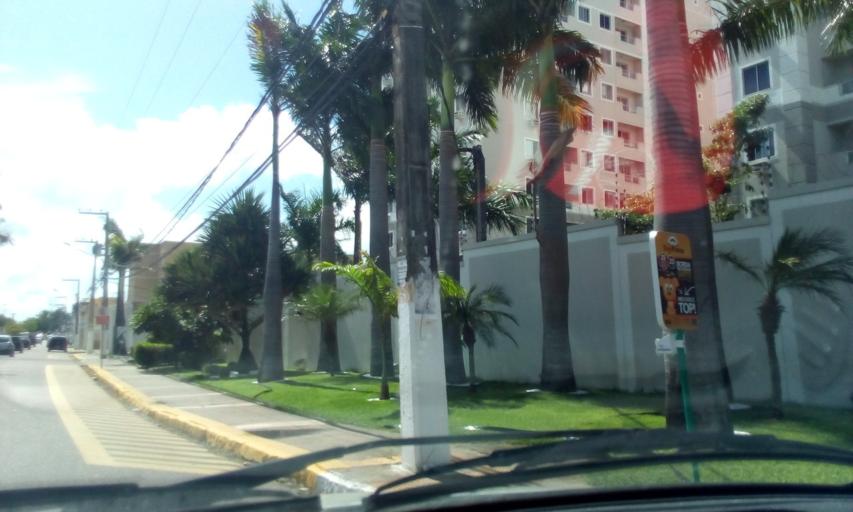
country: BR
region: Rio Grande do Norte
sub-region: Parnamirim
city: Parnamirim
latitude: -5.8838
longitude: -35.2023
